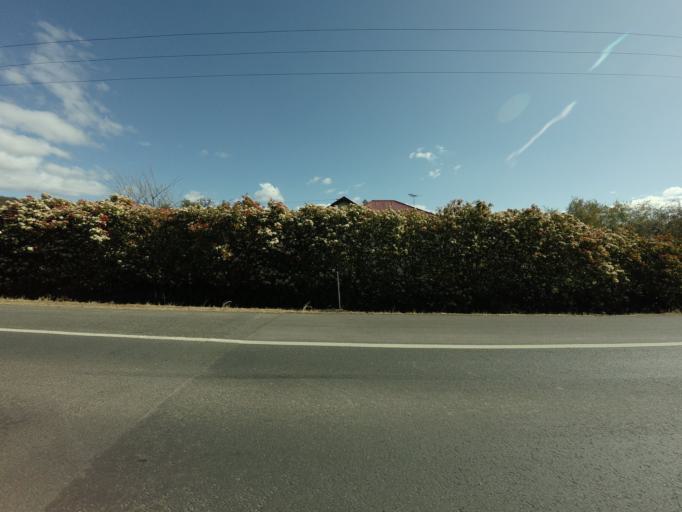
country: AU
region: Tasmania
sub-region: Derwent Valley
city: New Norfolk
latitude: -42.7755
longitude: 147.0368
